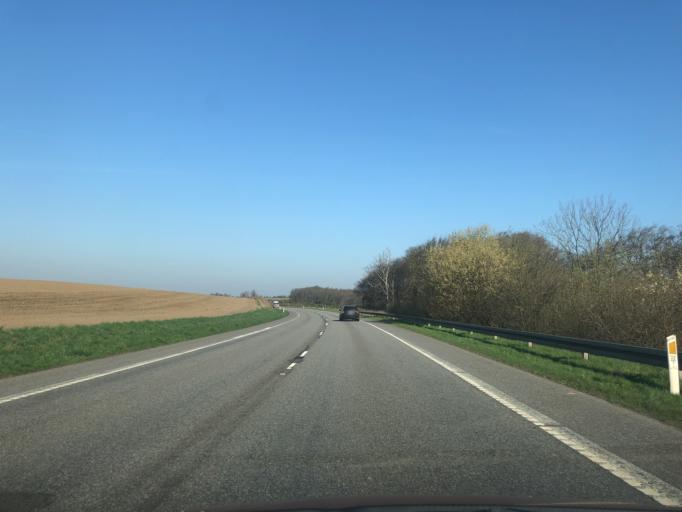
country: DK
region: Zealand
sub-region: Faxe Kommune
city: Haslev
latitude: 55.3025
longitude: 11.9939
